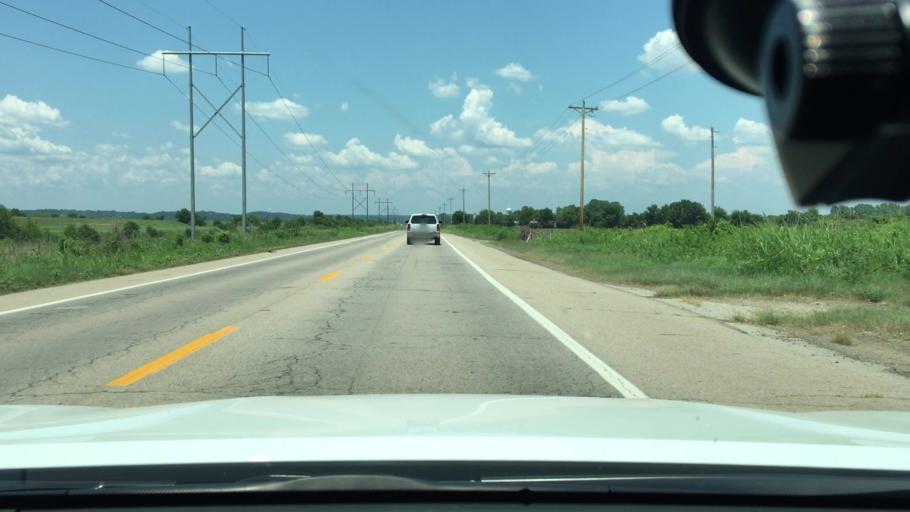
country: US
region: Arkansas
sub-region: Crawford County
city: Van Buren
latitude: 35.3957
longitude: -94.3303
